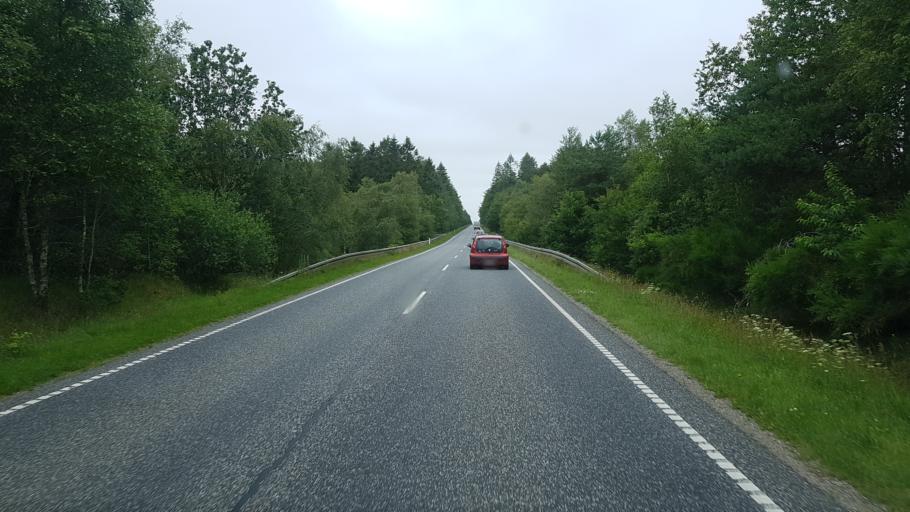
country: DK
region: Central Jutland
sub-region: Lemvig Kommune
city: Lemvig
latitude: 56.4634
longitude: 8.3254
